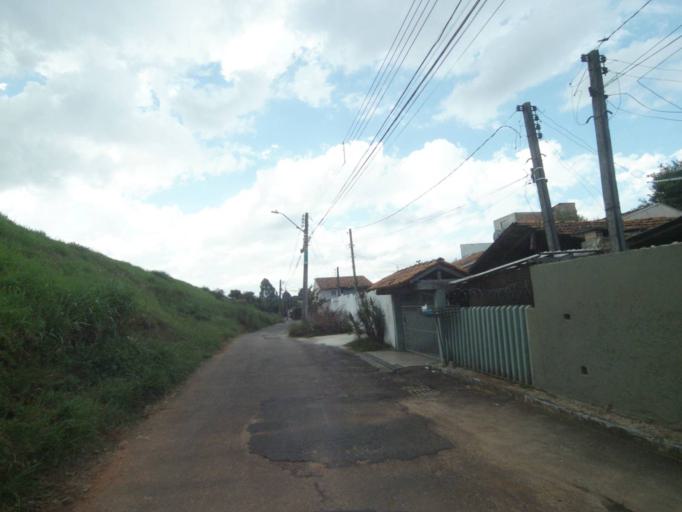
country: BR
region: Parana
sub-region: Pinhais
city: Pinhais
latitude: -25.4464
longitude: -49.2145
